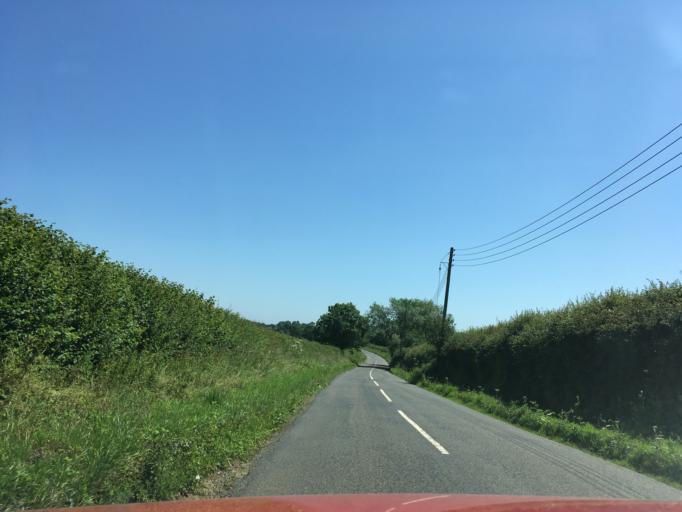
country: GB
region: England
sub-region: Milton Keynes
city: Calverton
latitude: 52.0035
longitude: -0.8590
